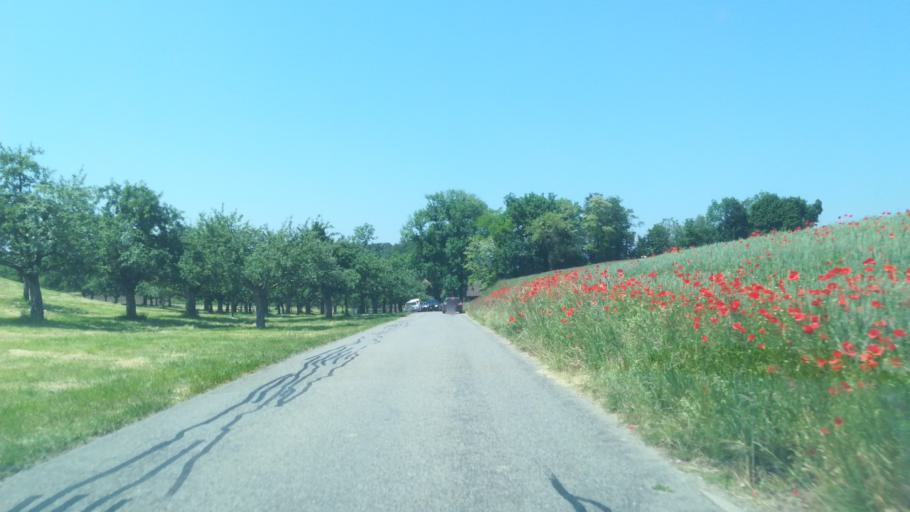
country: CH
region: Thurgau
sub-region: Frauenfeld District
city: Pfyn
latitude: 47.6284
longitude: 8.9278
